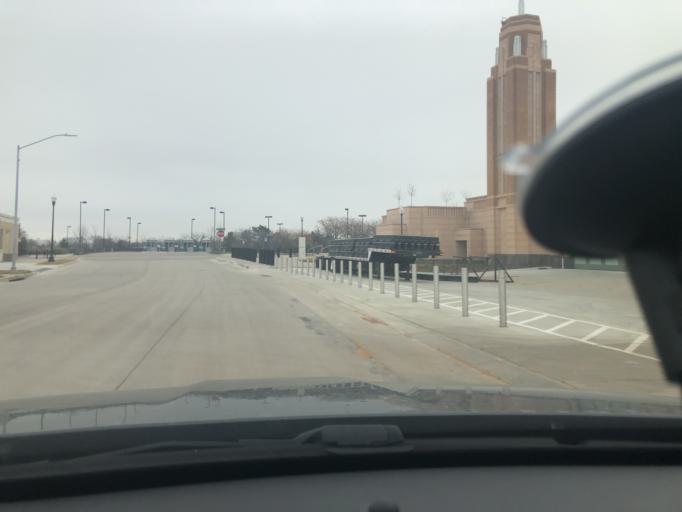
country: US
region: Texas
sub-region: Tarrant County
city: River Oaks
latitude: 32.7417
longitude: -97.3670
